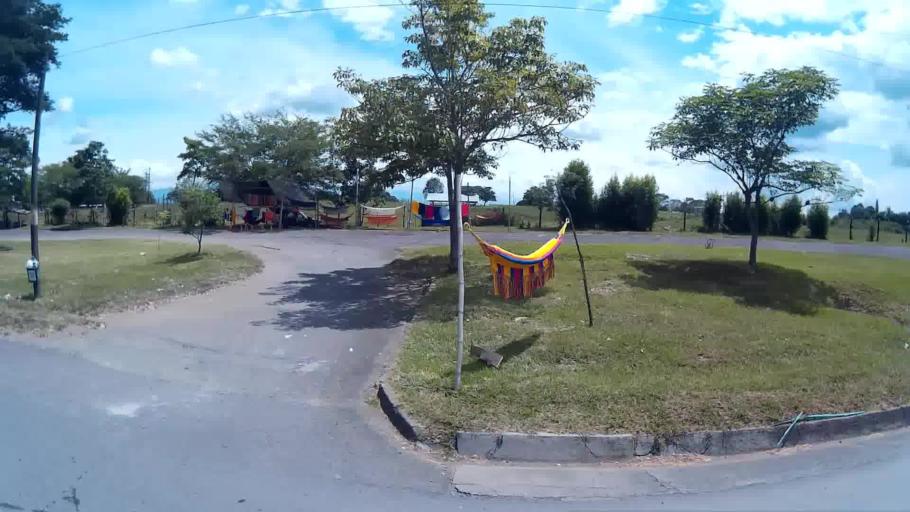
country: CO
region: Risaralda
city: Pereira
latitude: 4.8107
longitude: -75.8099
